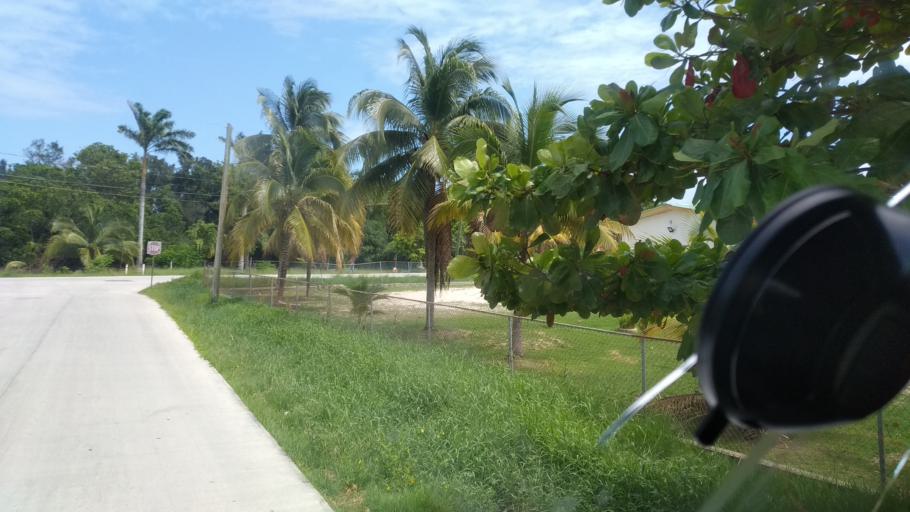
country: BZ
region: Belize
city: Belize City
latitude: 17.5124
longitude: -88.2009
